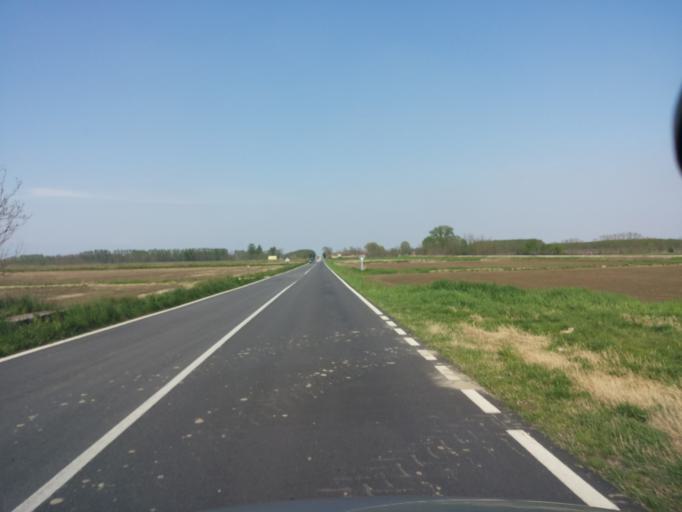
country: IT
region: Lombardy
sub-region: Provincia di Pavia
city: Zeme
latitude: 45.2054
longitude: 8.6392
